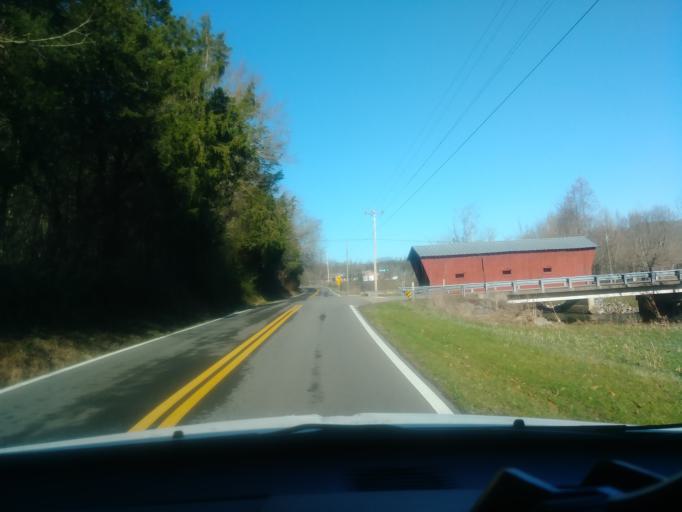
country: US
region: Tennessee
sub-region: Greene County
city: Mosheim
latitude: 36.1241
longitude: -83.0534
